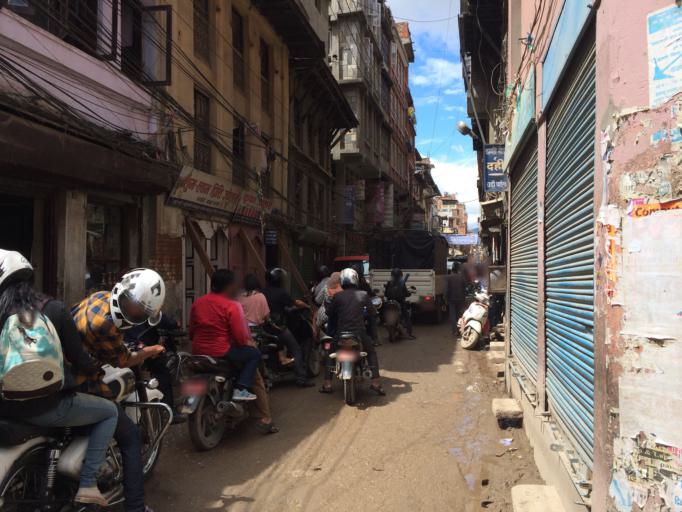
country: NP
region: Central Region
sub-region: Bagmati Zone
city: Kathmandu
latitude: 27.7079
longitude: 85.3073
